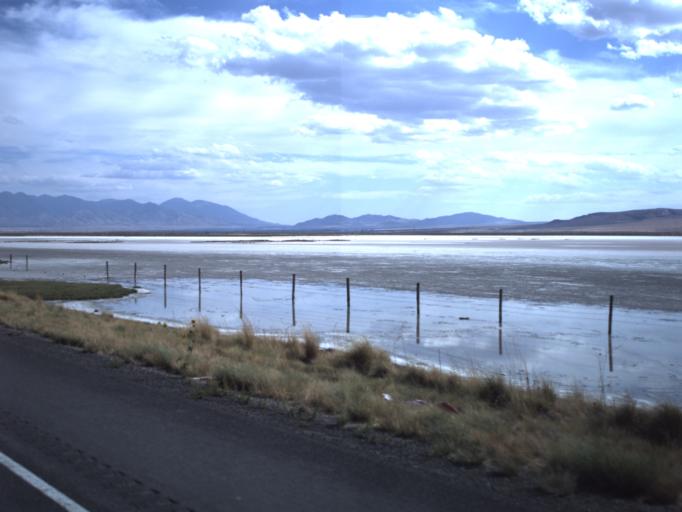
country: US
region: Utah
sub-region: Tooele County
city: Grantsville
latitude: 40.7200
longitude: -112.5554
